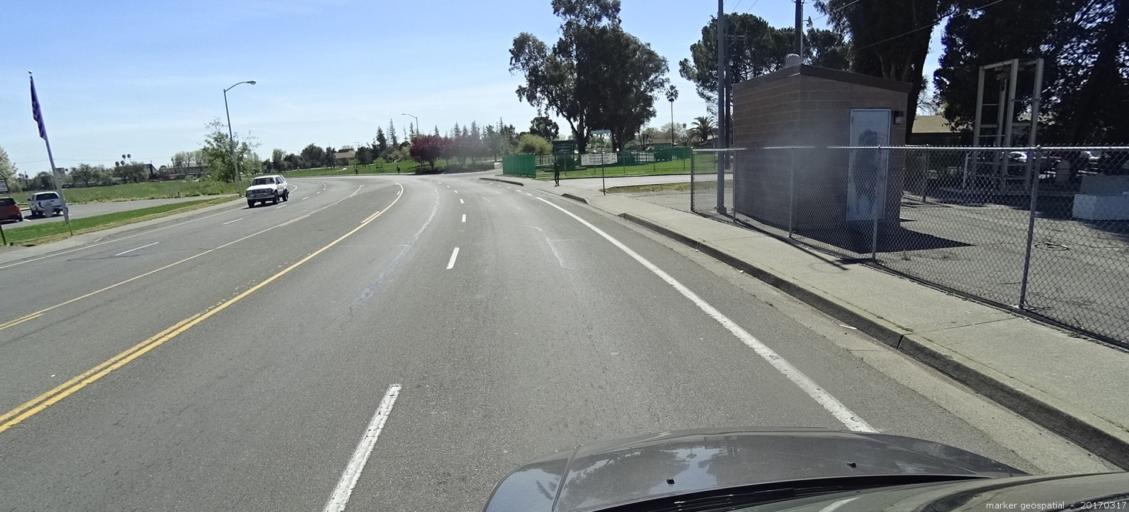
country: US
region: California
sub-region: Sacramento County
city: Parkway
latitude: 38.4941
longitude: -121.4828
